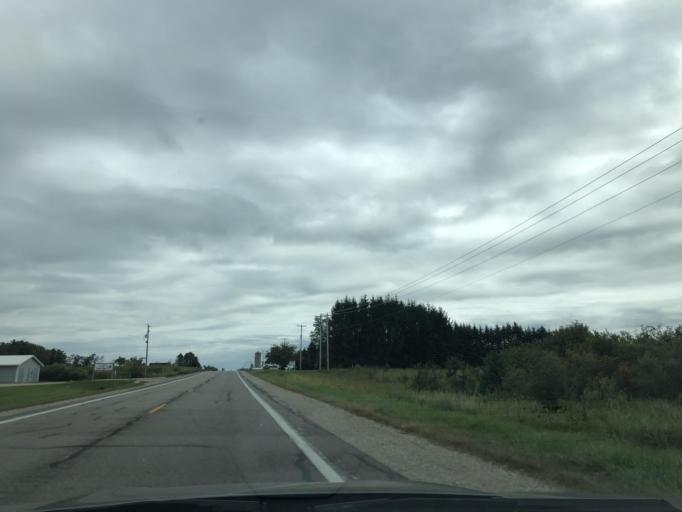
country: US
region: Michigan
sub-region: Missaukee County
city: Lake City
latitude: 44.1937
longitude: -85.1904
